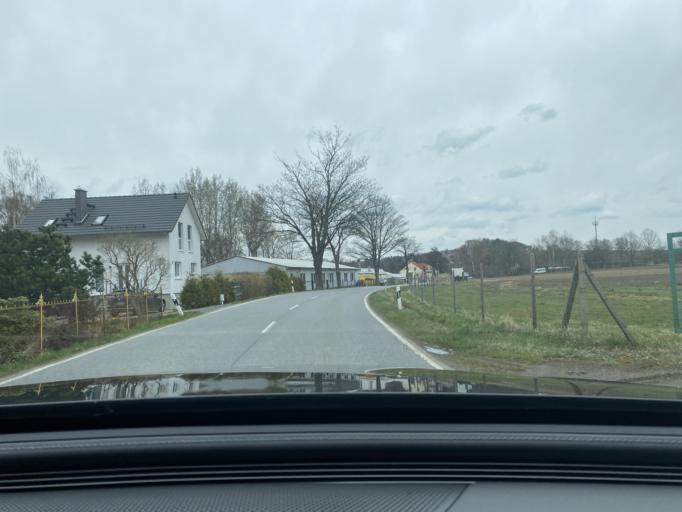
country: DE
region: Saxony
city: Stolpen
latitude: 51.0394
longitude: 14.0543
